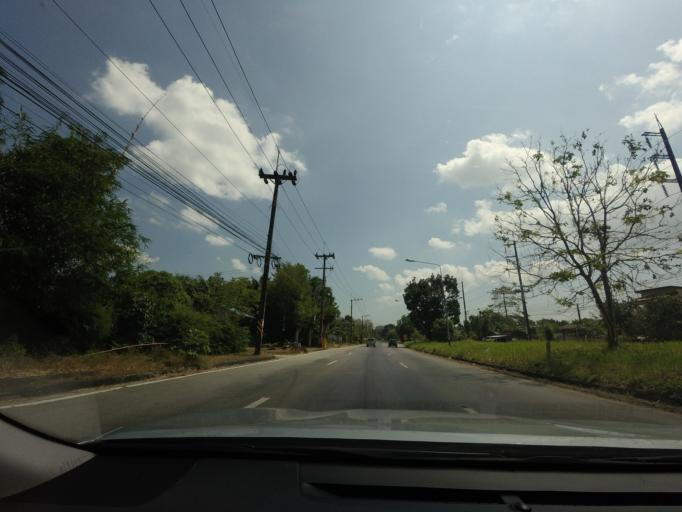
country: TH
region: Phangnga
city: Thai Mueang
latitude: 8.2724
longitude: 98.3264
